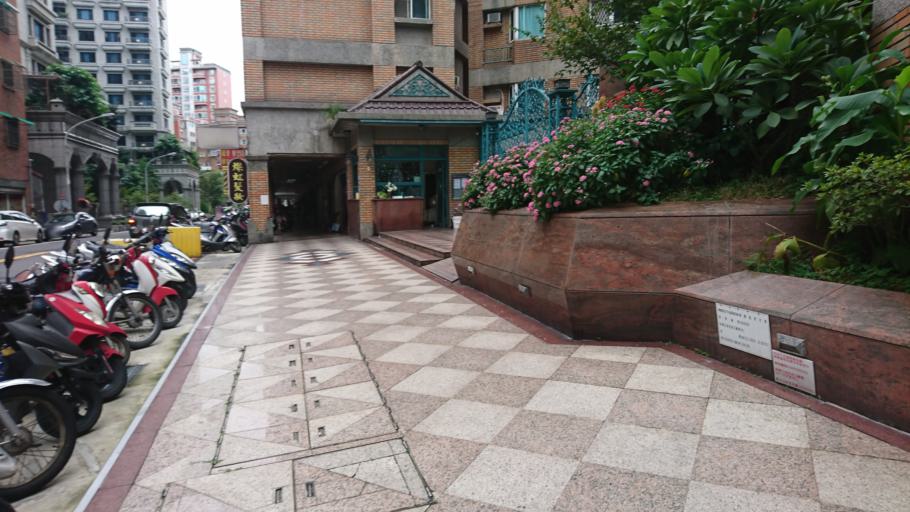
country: TW
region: Taiwan
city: Taoyuan City
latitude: 25.0578
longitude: 121.2961
